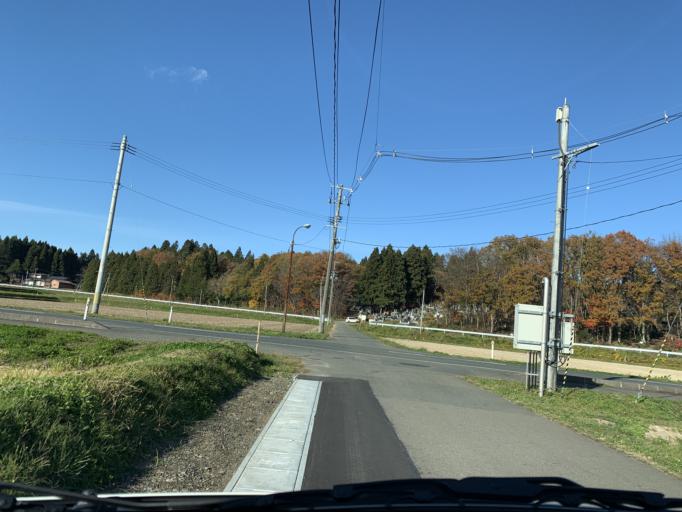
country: JP
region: Iwate
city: Kitakami
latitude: 39.2372
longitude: 141.0742
